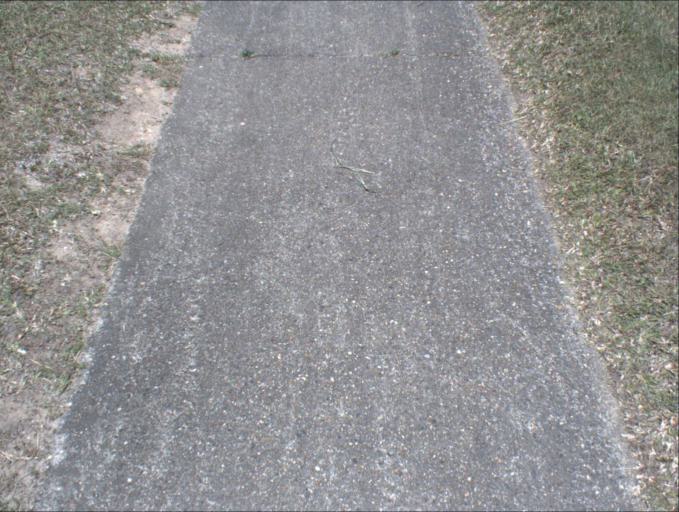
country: AU
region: Queensland
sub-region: Logan
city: Springwood
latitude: -27.6026
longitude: 153.1364
